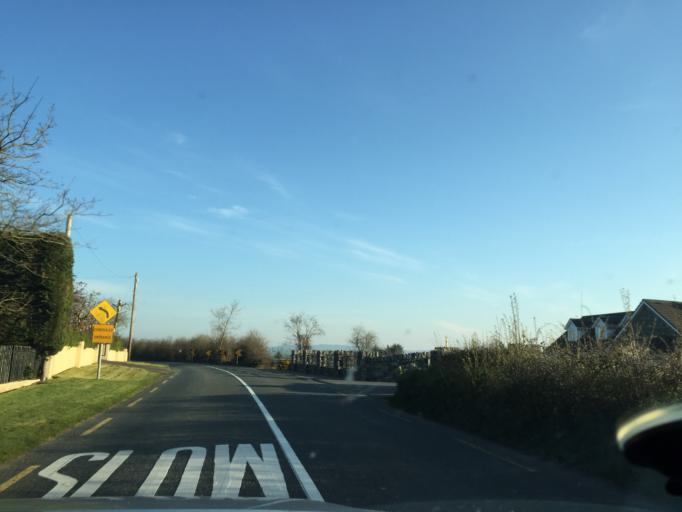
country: IE
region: Munster
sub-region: Ciarrai
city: Cill Airne
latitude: 52.0843
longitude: -9.5263
